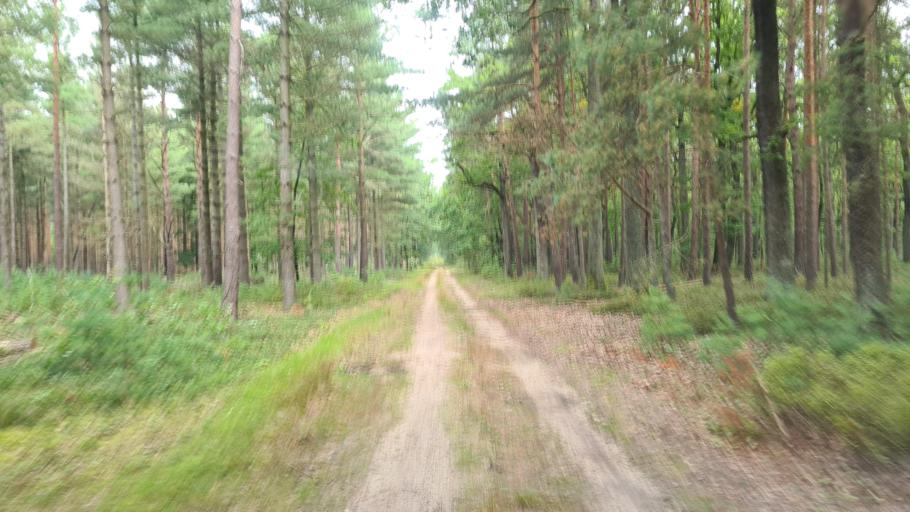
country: DE
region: Brandenburg
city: Hohenbucko
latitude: 51.7763
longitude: 13.5506
